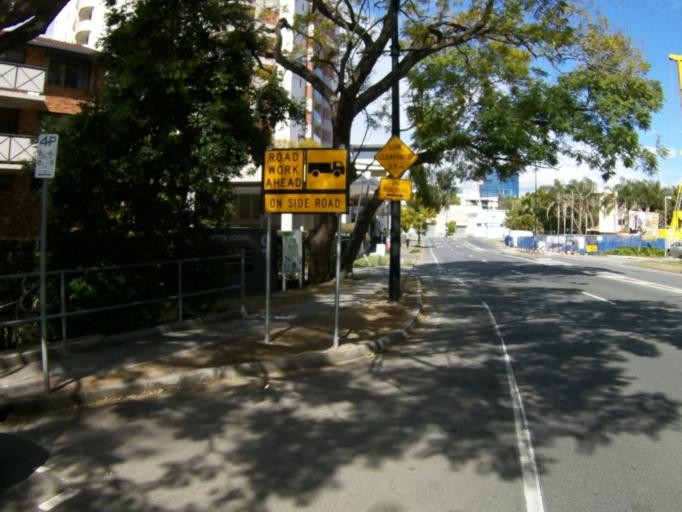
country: AU
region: Queensland
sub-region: Brisbane
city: Toowong
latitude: -27.4808
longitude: 152.9956
